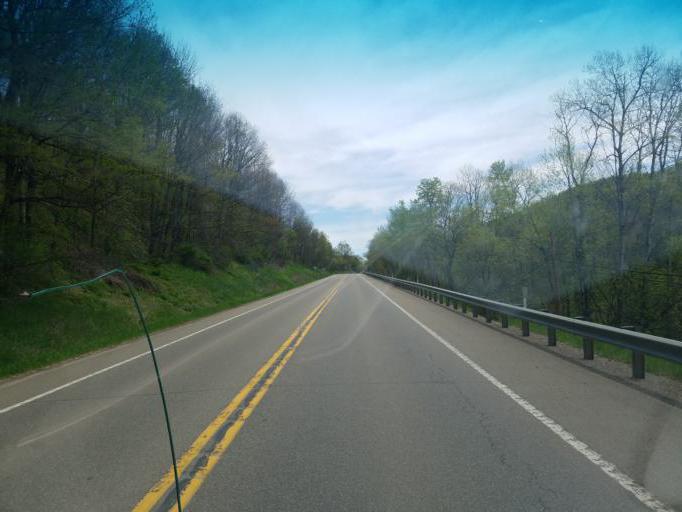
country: US
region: Pennsylvania
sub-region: Potter County
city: Galeton
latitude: 41.7383
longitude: -77.6322
